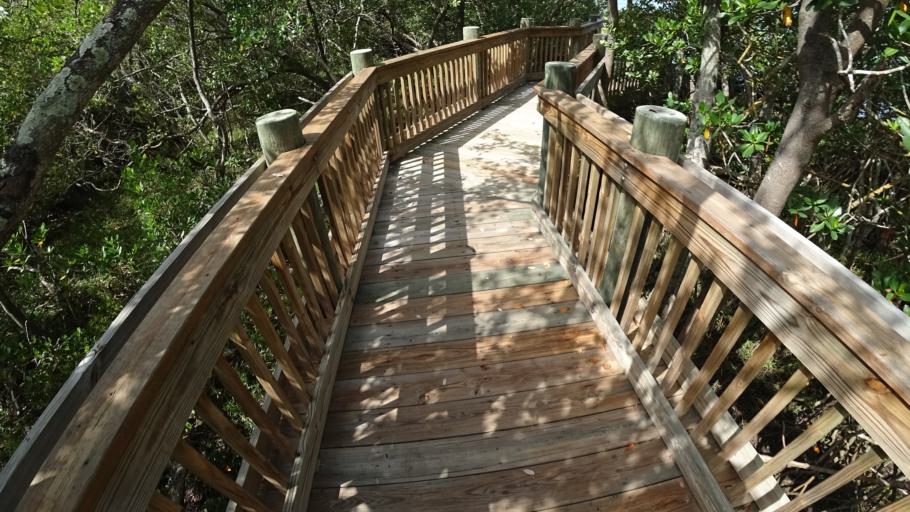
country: US
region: Florida
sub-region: Manatee County
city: Holmes Beach
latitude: 27.4950
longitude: -82.6870
